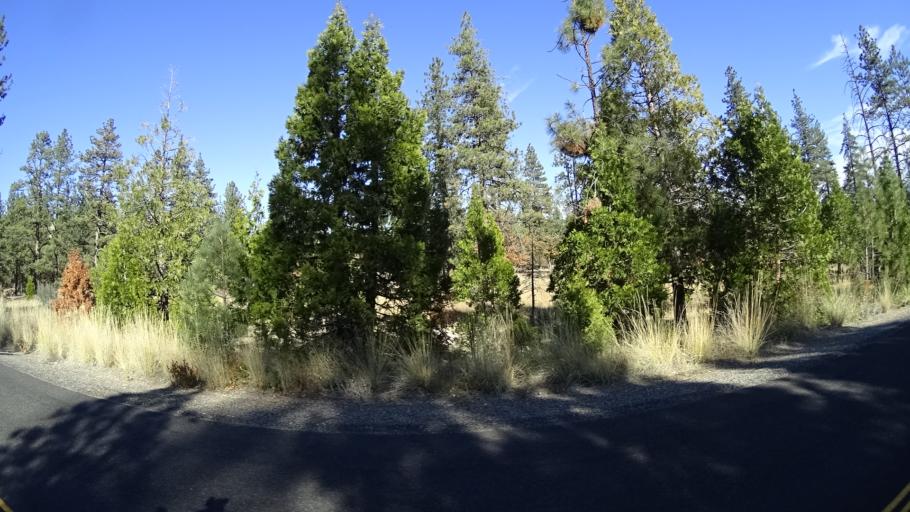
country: US
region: California
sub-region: Siskiyou County
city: Weed
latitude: 41.4363
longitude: -122.4643
